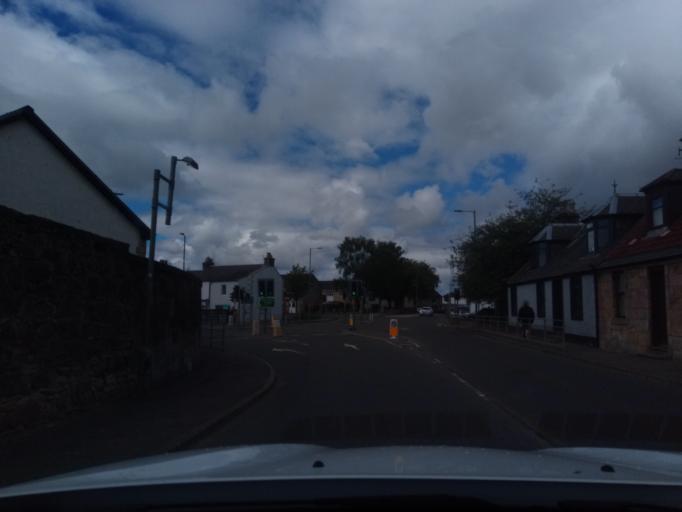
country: GB
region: Scotland
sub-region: Fife
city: Kincardine
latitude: 56.0689
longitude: -3.7161
